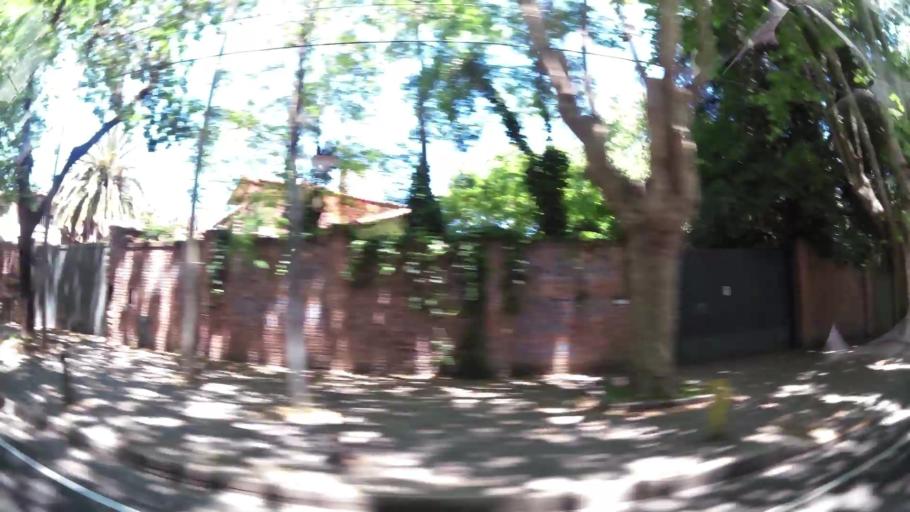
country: AR
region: Buenos Aires
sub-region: Partido de San Isidro
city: San Isidro
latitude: -34.4478
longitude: -58.5393
